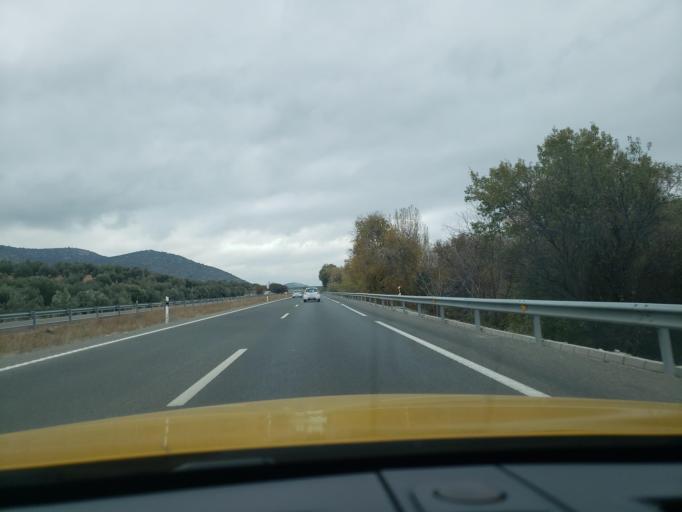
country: ES
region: Andalusia
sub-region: Provincia de Granada
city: Deifontes
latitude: 37.3782
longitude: -3.5903
